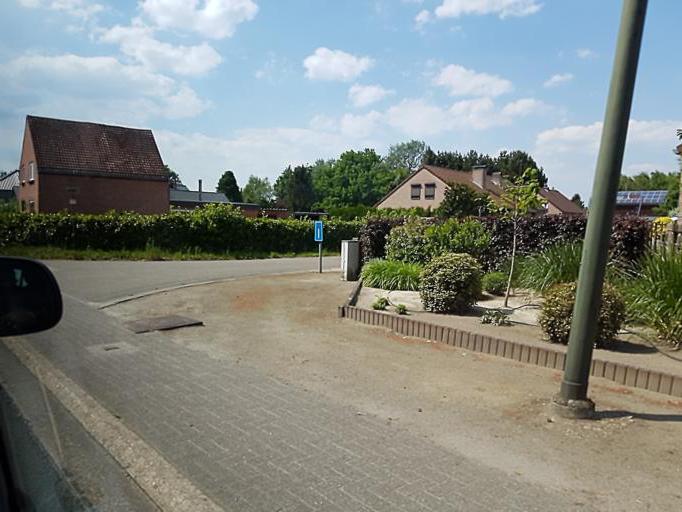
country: BE
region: Flanders
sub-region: Provincie Limburg
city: Neerpelt
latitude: 51.2190
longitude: 5.4894
